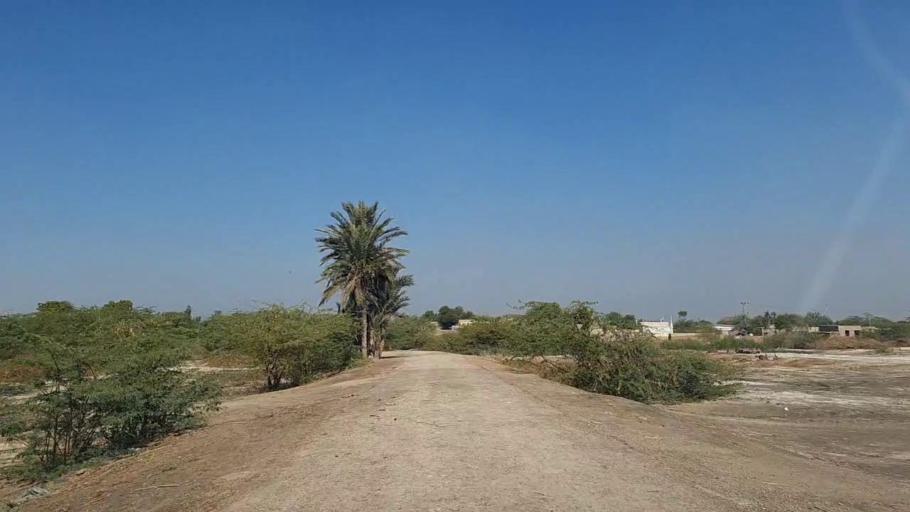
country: PK
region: Sindh
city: Nawabshah
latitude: 26.3406
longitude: 68.3545
